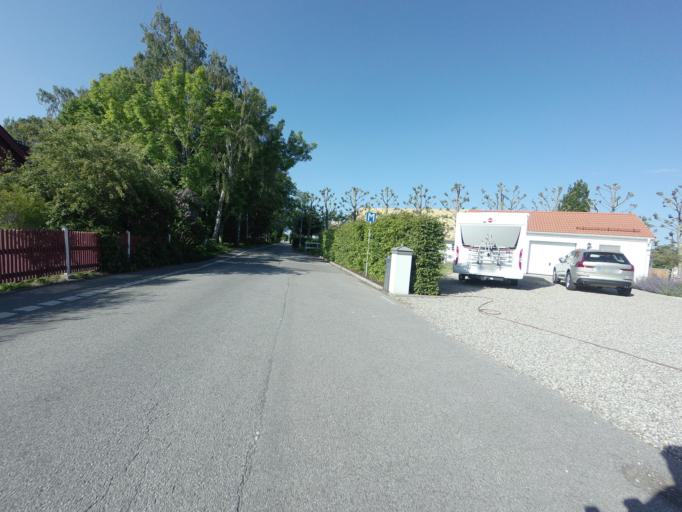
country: SE
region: Skane
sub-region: Trelleborgs Kommun
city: Skare
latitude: 55.4139
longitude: 13.0095
